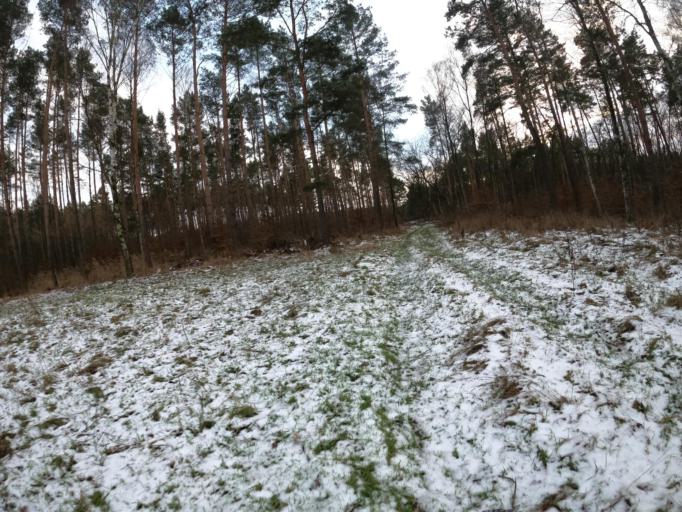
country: PL
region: Lubusz
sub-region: Powiat slubicki
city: Cybinka
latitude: 52.1862
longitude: 14.8722
